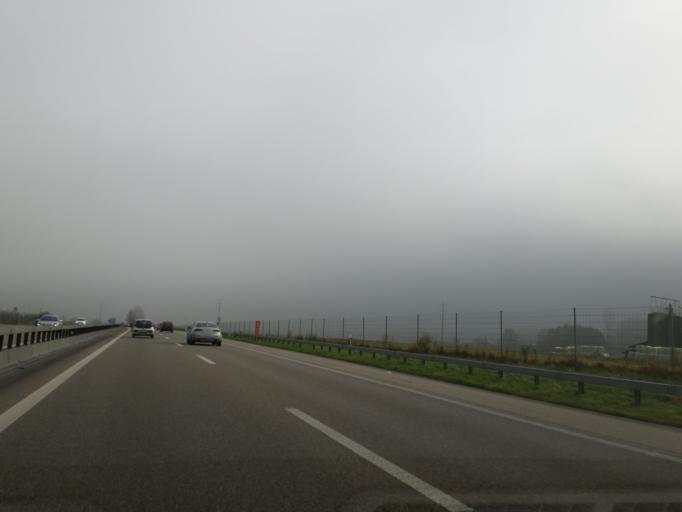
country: CH
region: Bern
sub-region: Oberaargau
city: Niederbipp
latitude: 47.2565
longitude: 7.6890
